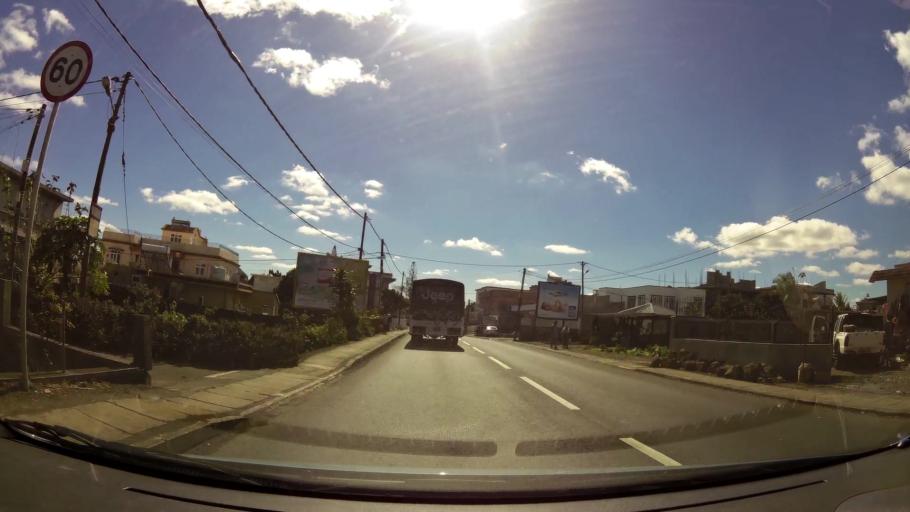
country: MU
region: Plaines Wilhems
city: Vacoas
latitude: -20.2902
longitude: 57.4819
